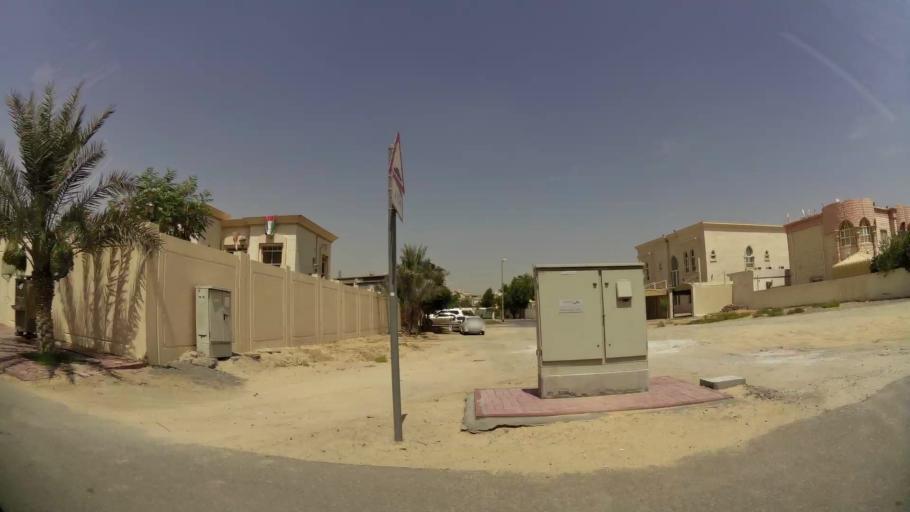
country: AE
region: Ash Shariqah
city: Sharjah
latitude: 25.1807
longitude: 55.4152
